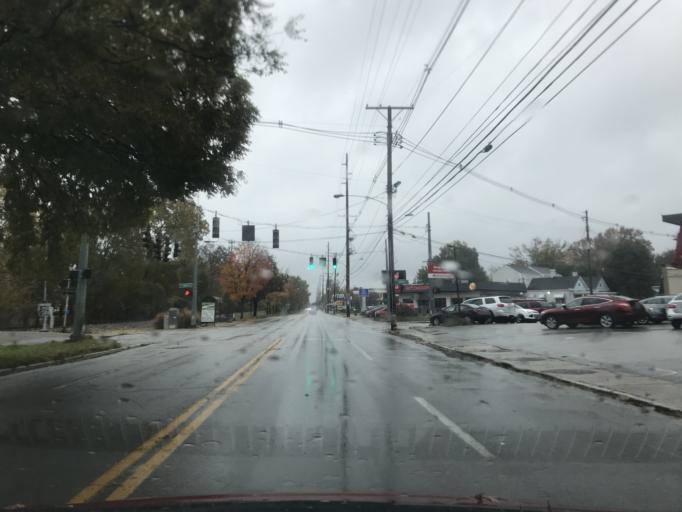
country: US
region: Kentucky
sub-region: Jefferson County
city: Saint Matthews
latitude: 38.2541
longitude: -85.6709
